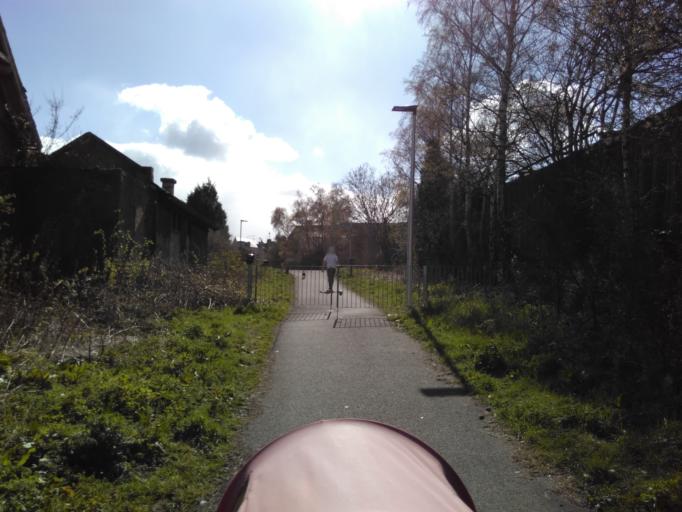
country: GB
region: Scotland
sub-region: Midlothian
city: Loanhead
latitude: 55.8789
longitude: -3.1465
